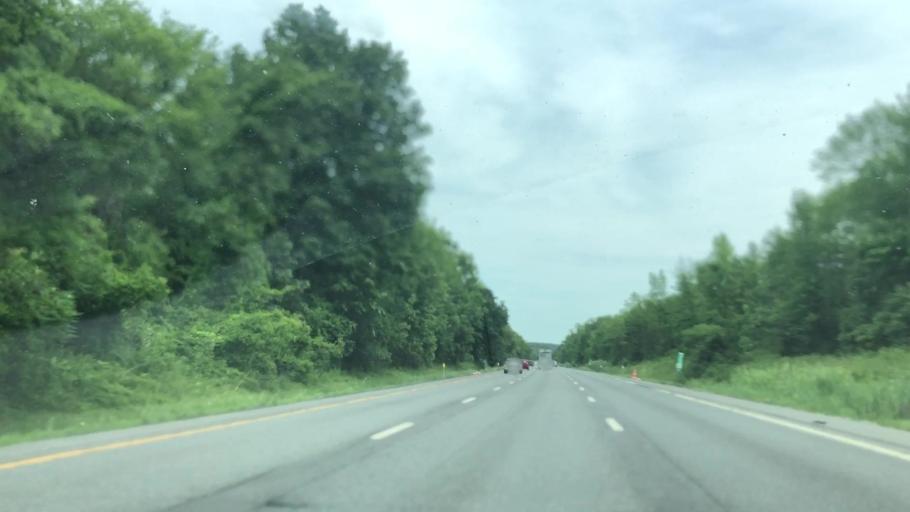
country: US
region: New York
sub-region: Saratoga County
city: Saratoga Springs
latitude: 43.0316
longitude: -73.7812
